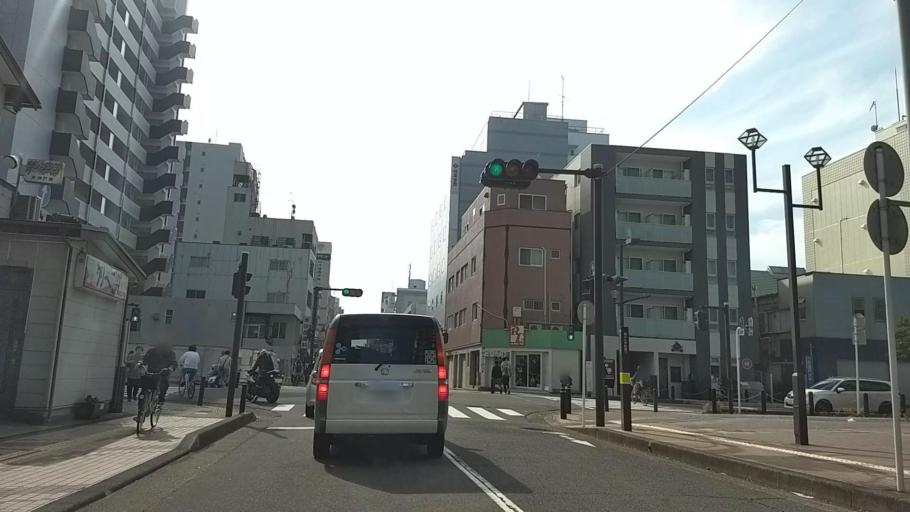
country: JP
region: Kanagawa
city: Atsugi
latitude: 35.4440
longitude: 139.3634
